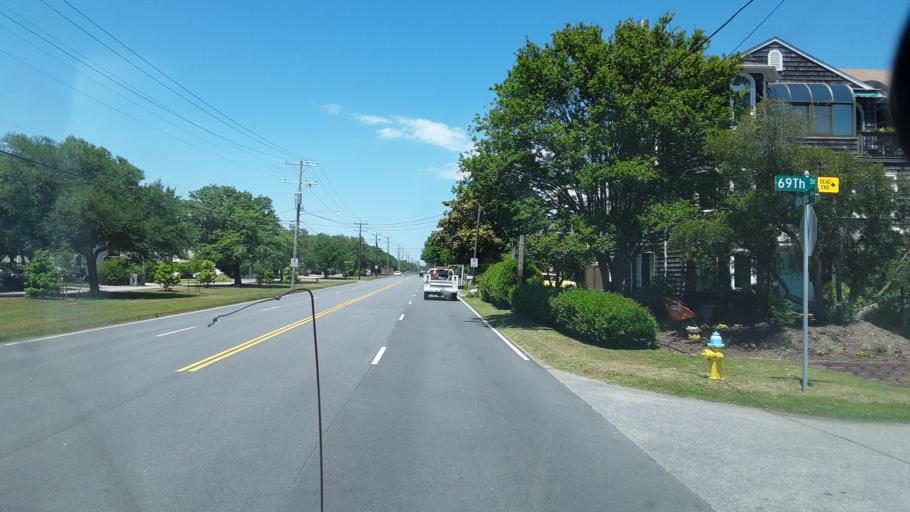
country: US
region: Virginia
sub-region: City of Virginia Beach
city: Virginia Beach
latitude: 36.8945
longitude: -75.9896
